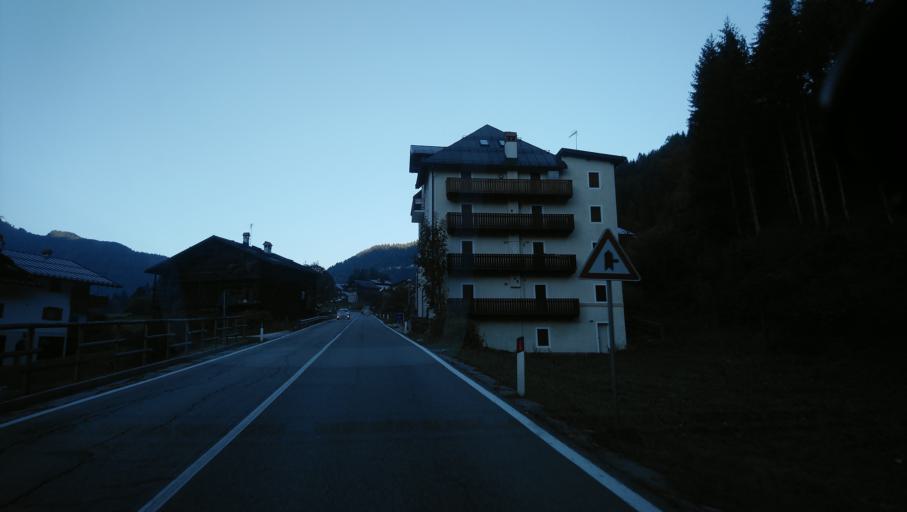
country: IT
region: Veneto
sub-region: Provincia di Belluno
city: Vallada Agordina
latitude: 46.3643
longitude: 11.9460
